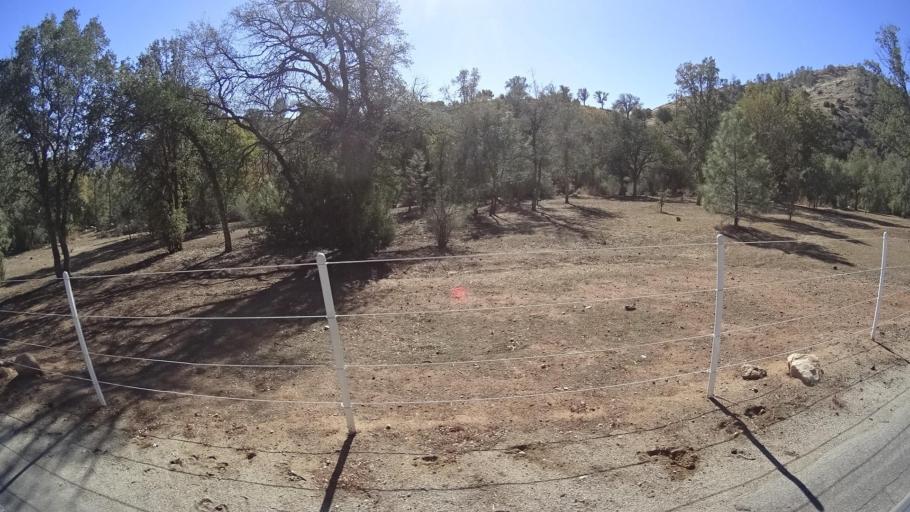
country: US
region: California
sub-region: Kern County
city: Wofford Heights
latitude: 35.7035
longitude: -118.4644
